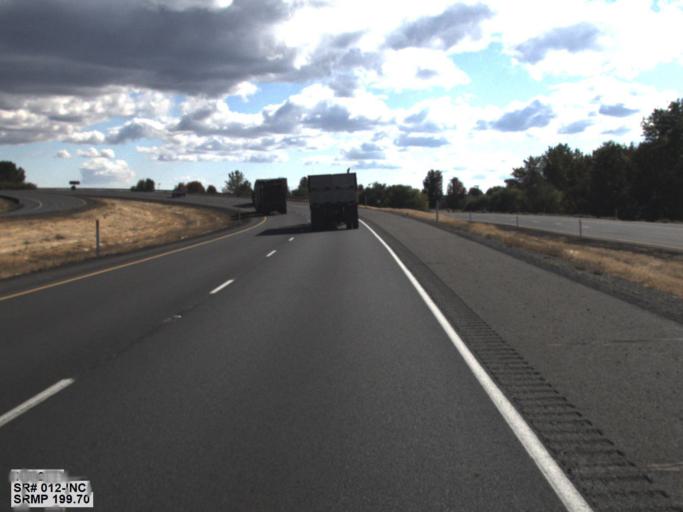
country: US
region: Washington
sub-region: Yakima County
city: West Valley
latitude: 46.6233
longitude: -120.5692
